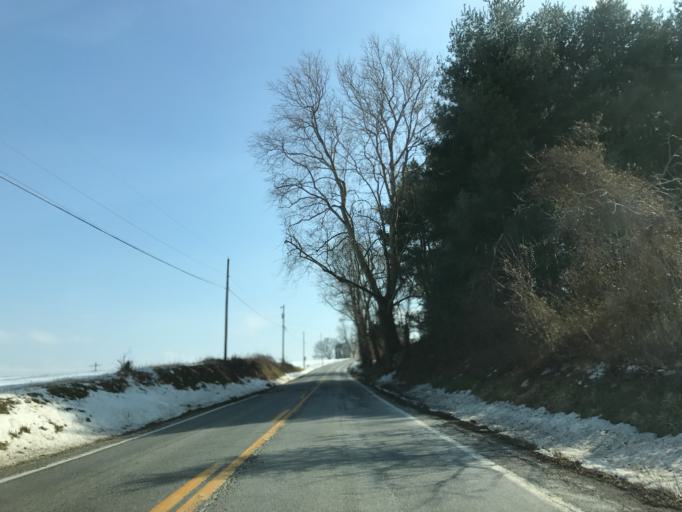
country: US
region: Pennsylvania
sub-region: York County
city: Susquehanna Trails
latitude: 39.6952
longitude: -76.3901
